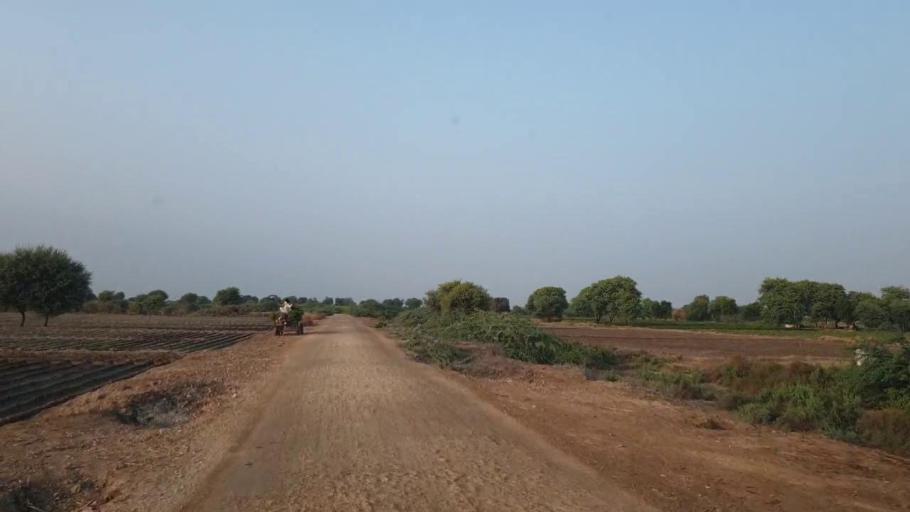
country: PK
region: Sindh
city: Tando Ghulam Ali
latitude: 25.0651
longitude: 68.9605
